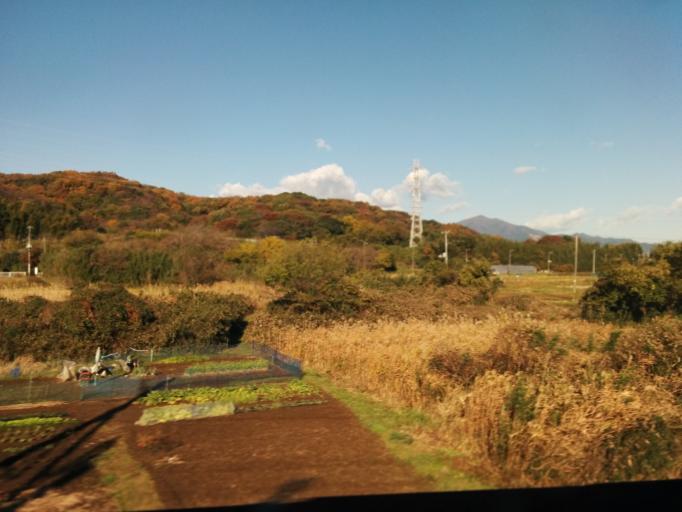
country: JP
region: Kanagawa
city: Oiso
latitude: 35.3296
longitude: 139.2946
